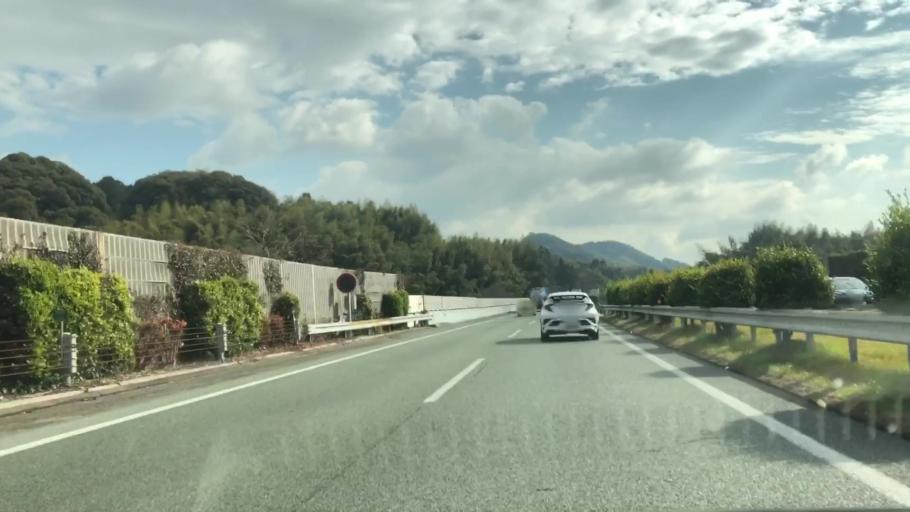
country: JP
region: Fukuoka
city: Setakamachi-takayanagi
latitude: 33.1130
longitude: 130.5304
